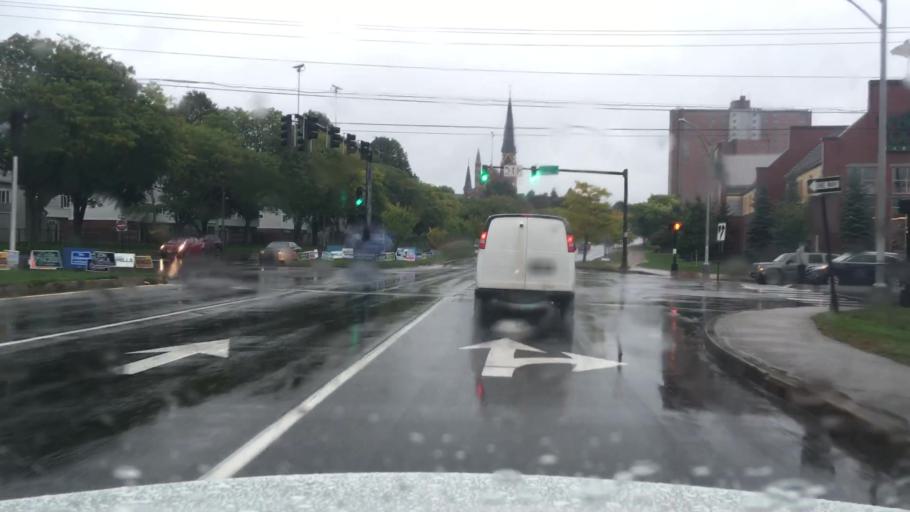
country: US
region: Maine
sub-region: Cumberland County
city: Portland
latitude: 43.6644
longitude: -70.2590
